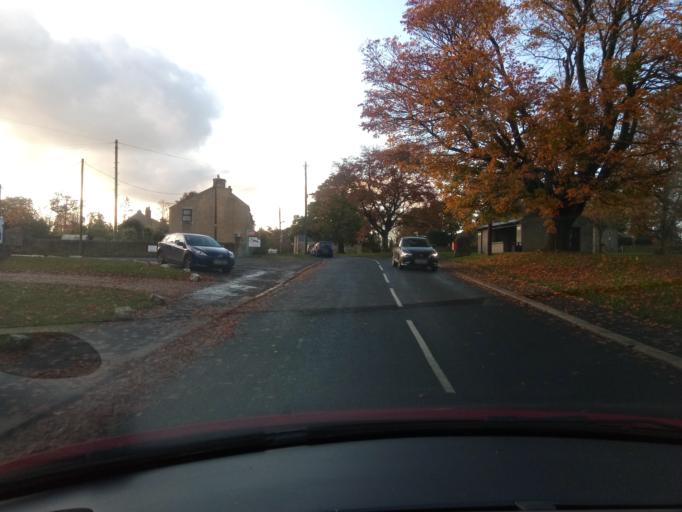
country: GB
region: England
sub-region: County Durham
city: Hamsterley
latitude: 54.6747
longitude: -1.8220
